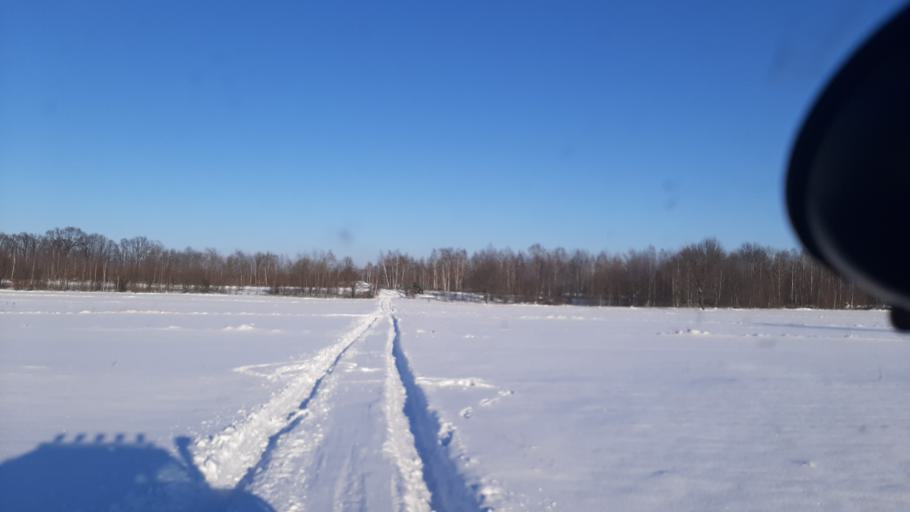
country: PL
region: Lublin Voivodeship
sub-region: Powiat lubelski
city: Jastkow
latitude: 51.3872
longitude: 22.4316
